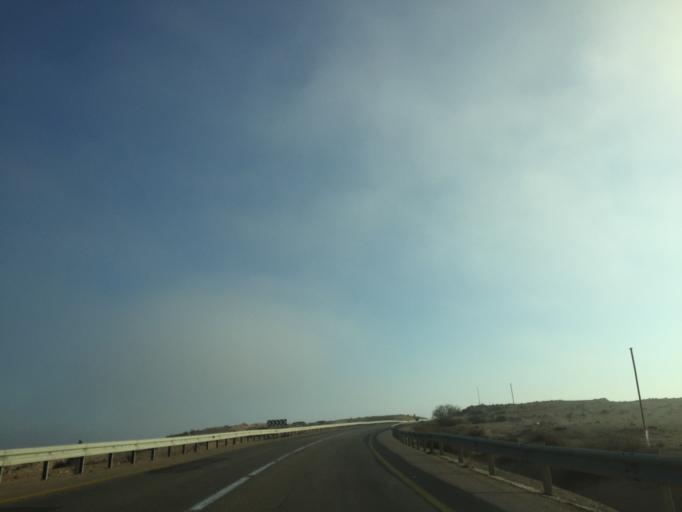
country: IL
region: Southern District
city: Yeroham
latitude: 30.9962
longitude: 34.9251
